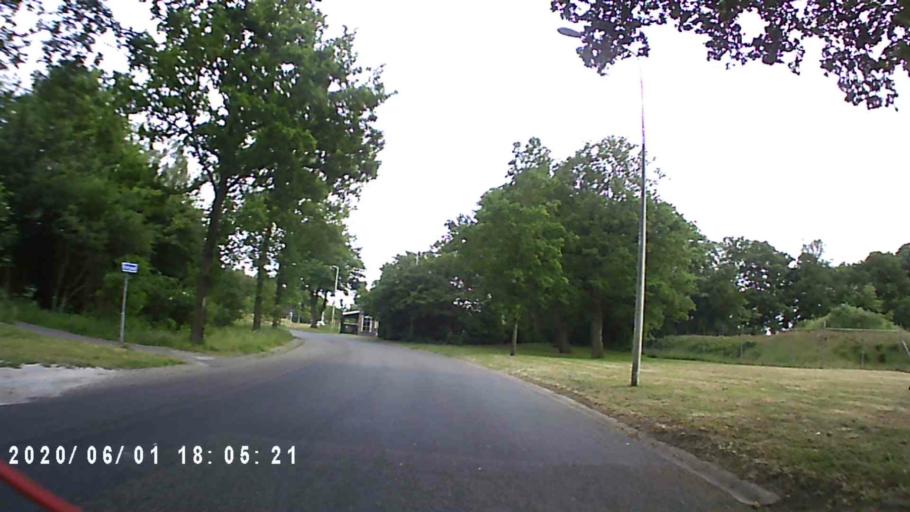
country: NL
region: Friesland
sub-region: Gemeente Tytsjerksteradiel
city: Sumar
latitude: 53.1797
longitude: 5.9941
